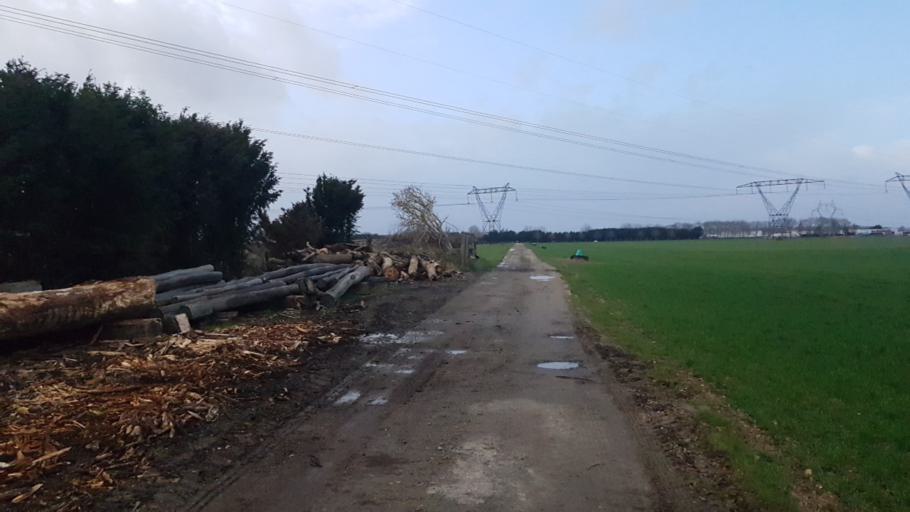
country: FR
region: Ile-de-France
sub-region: Departement de l'Essonne
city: Cheptainville
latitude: 48.5611
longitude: 2.2808
